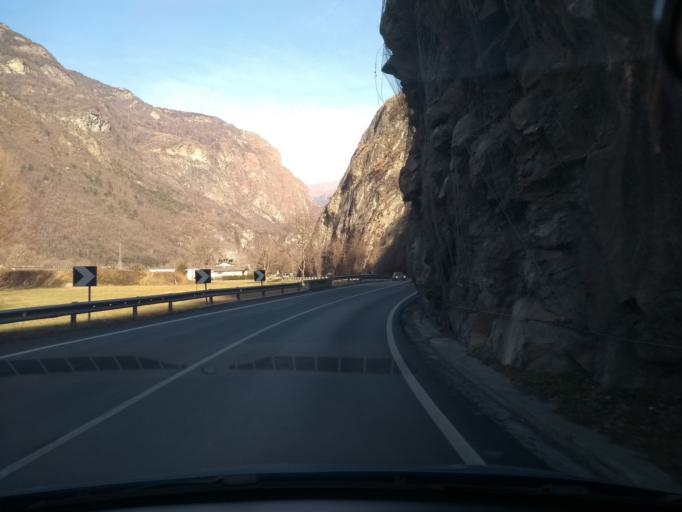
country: IT
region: Aosta Valley
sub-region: Valle d'Aosta
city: Montjovet
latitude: 45.6957
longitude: 7.6707
